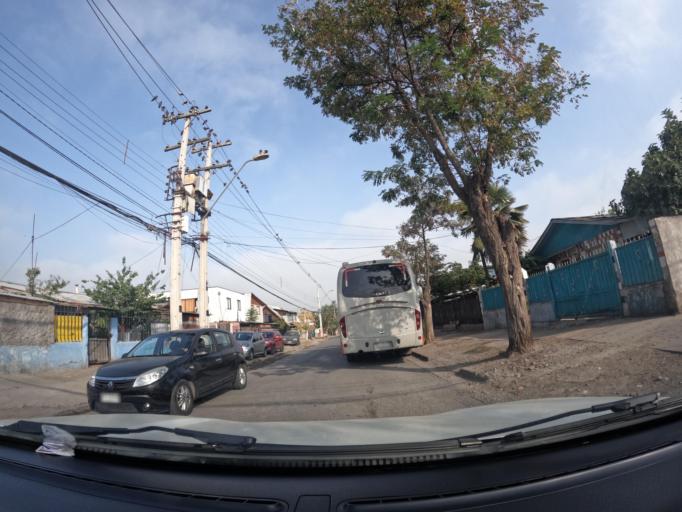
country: CL
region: Santiago Metropolitan
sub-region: Provincia de Santiago
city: Villa Presidente Frei, Nunoa, Santiago, Chile
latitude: -33.4740
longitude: -70.5613
